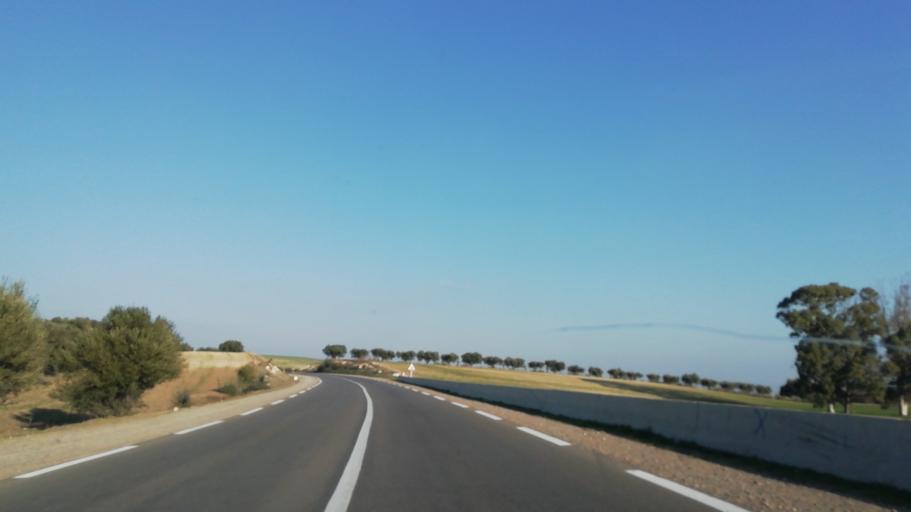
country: DZ
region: Sidi Bel Abbes
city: Sidi Bel Abbes
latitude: 35.1625
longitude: -0.8659
